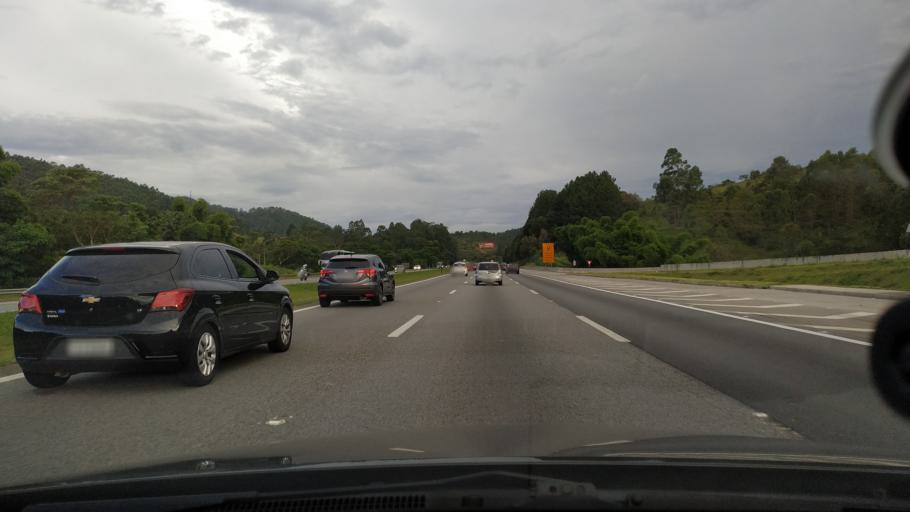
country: BR
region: Sao Paulo
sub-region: Pirapora Do Bom Jesus
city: Pirapora do Bom Jesus
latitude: -23.4595
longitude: -47.0450
